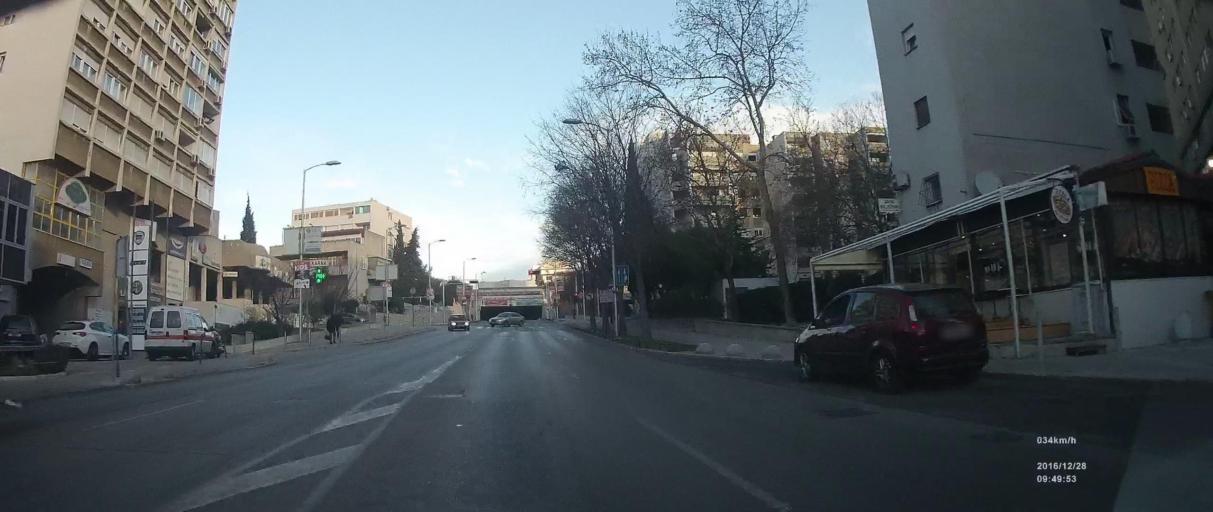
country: HR
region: Splitsko-Dalmatinska
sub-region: Grad Split
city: Split
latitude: 43.5058
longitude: 16.4562
